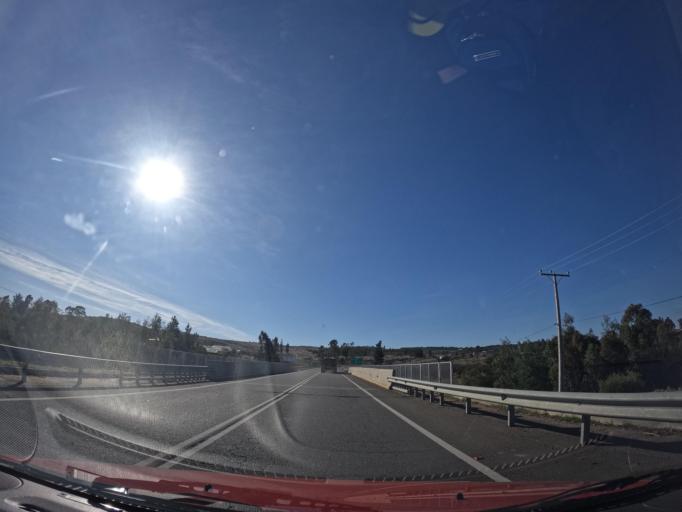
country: CL
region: Maule
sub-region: Provincia de Cauquenes
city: Cauquenes
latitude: -35.9446
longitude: -72.2005
